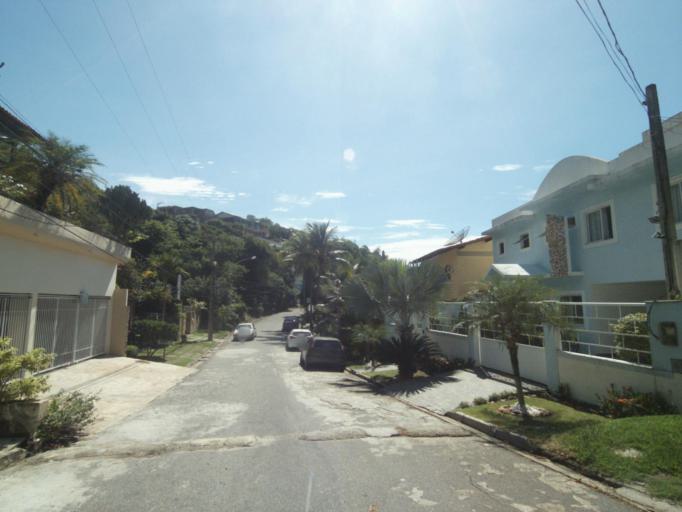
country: BR
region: Rio de Janeiro
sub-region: Niteroi
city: Niteroi
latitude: -22.9570
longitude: -43.0673
